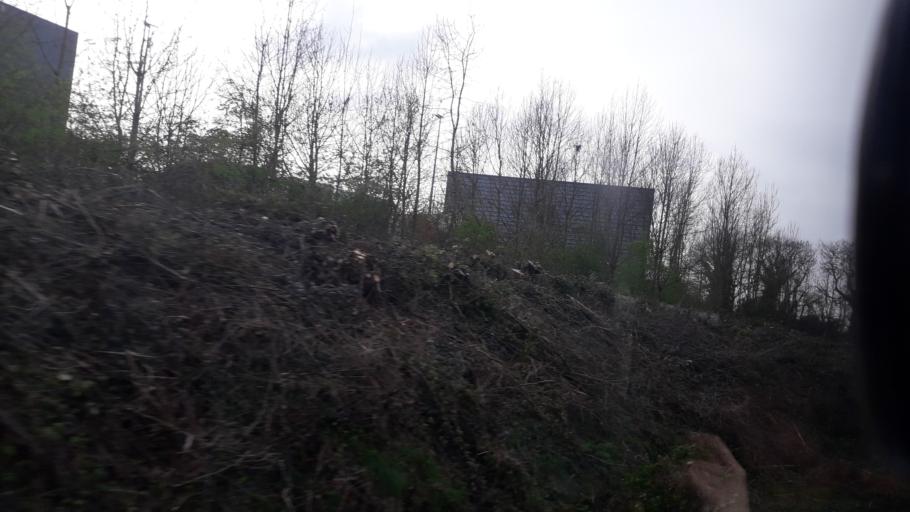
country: IE
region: Leinster
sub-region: Kildare
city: Kilcock
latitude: 53.4100
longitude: -6.6862
